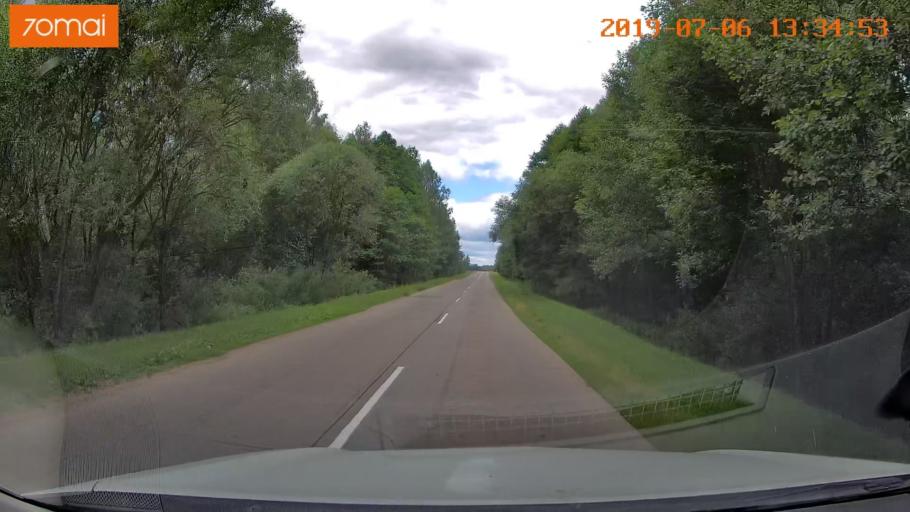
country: BY
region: Minsk
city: Enyerhyetykaw
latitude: 53.6779
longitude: 26.8906
